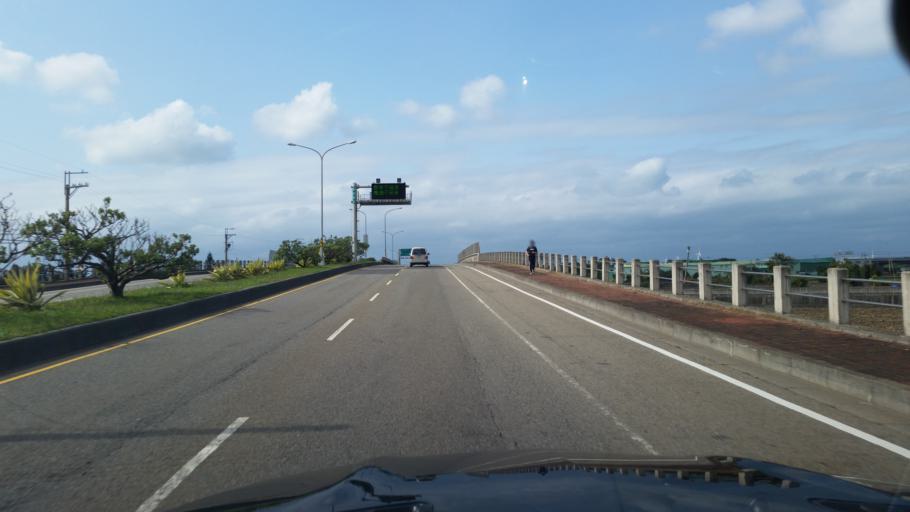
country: TW
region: Taiwan
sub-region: Miaoli
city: Miaoli
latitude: 24.6737
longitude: 120.8515
